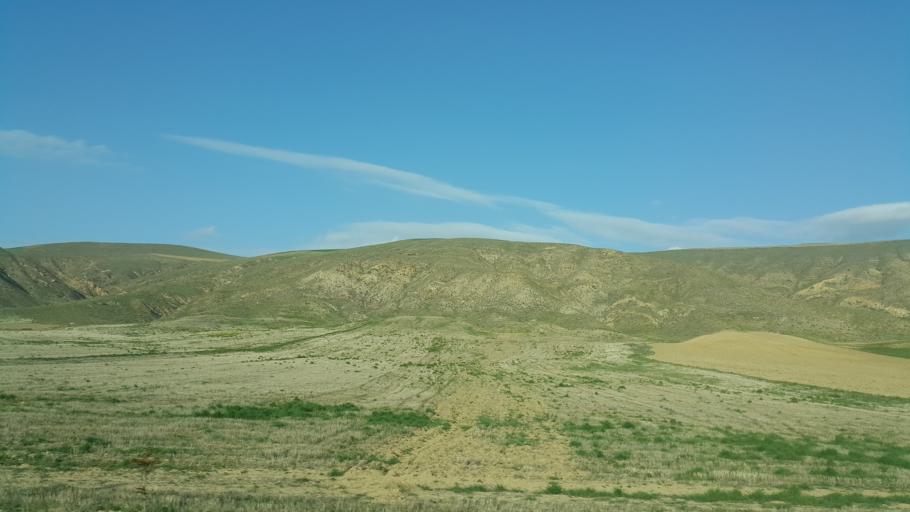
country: TR
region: Ankara
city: Sereflikochisar
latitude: 39.0337
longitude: 33.4456
